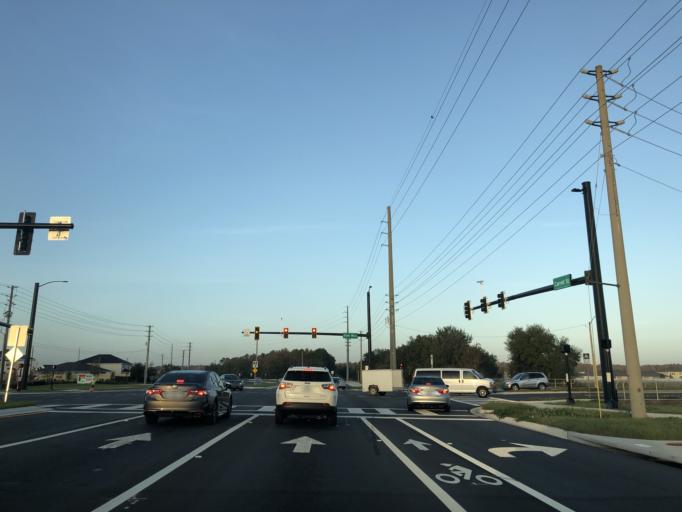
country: US
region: Florida
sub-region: Osceola County
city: Kissimmee
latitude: 28.3254
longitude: -81.4362
